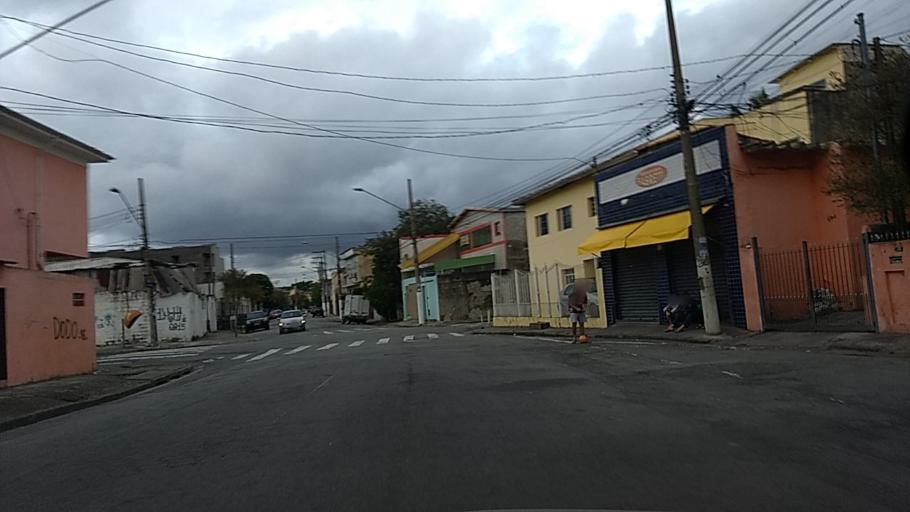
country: BR
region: Sao Paulo
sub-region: Sao Paulo
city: Sao Paulo
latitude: -23.5083
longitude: -46.6037
